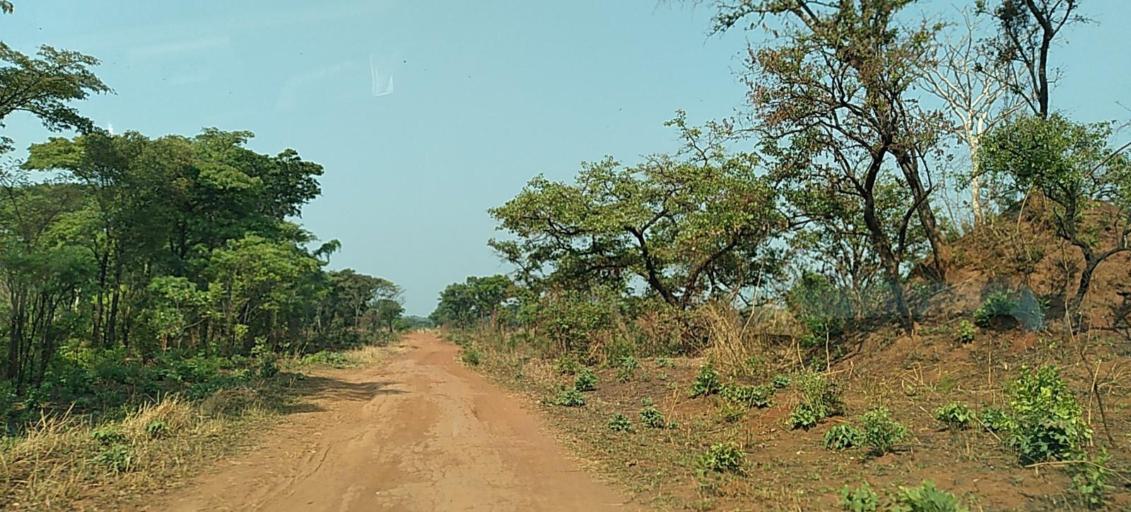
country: ZM
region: Copperbelt
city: Chingola
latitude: -12.8846
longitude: 27.4245
